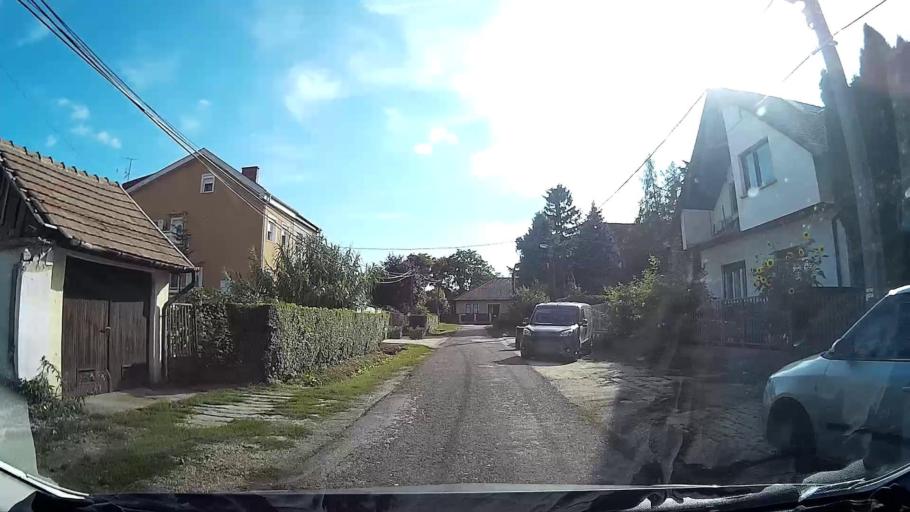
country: HU
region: Pest
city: Pomaz
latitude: 47.6372
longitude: 19.0325
